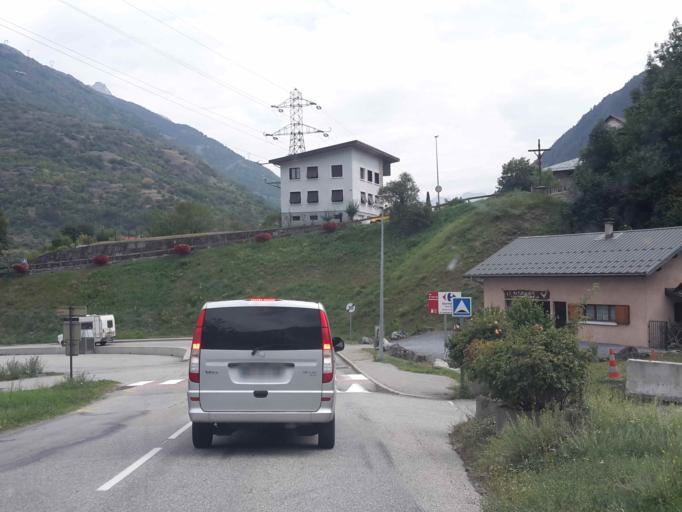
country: FR
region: Rhone-Alpes
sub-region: Departement de la Savoie
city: Saint-Michel-de-Maurienne
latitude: 45.2125
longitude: 6.4666
